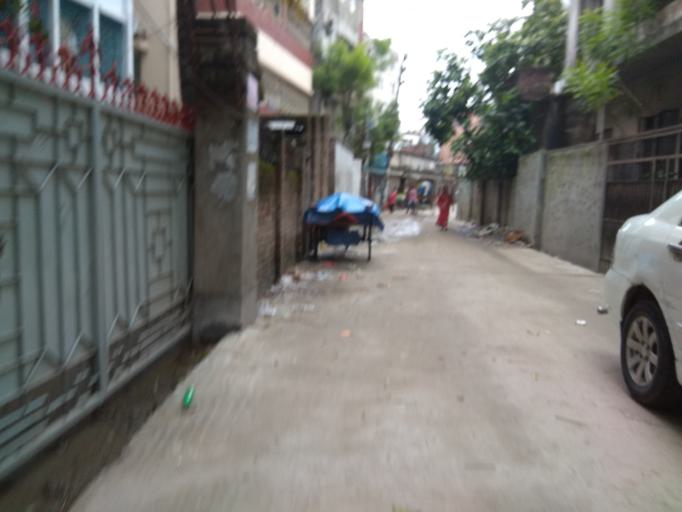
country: BD
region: Dhaka
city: Azimpur
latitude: 23.7946
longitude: 90.3693
